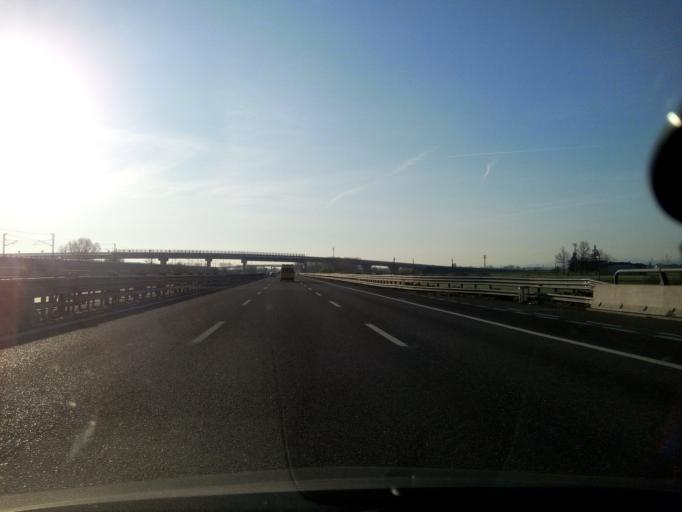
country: IT
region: Emilia-Romagna
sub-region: Provincia di Piacenza
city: Alseno
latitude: 44.9358
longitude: 9.9671
